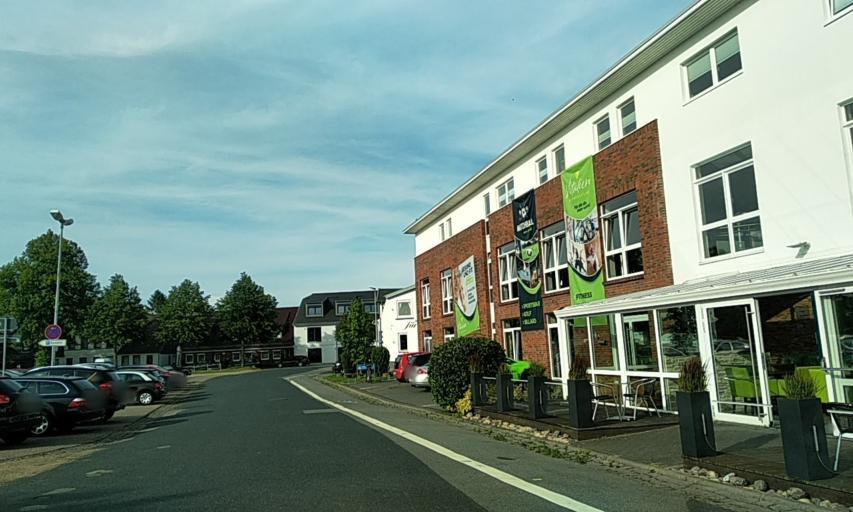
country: DE
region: Schleswig-Holstein
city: Schleswig
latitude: 54.5214
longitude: 9.5638
